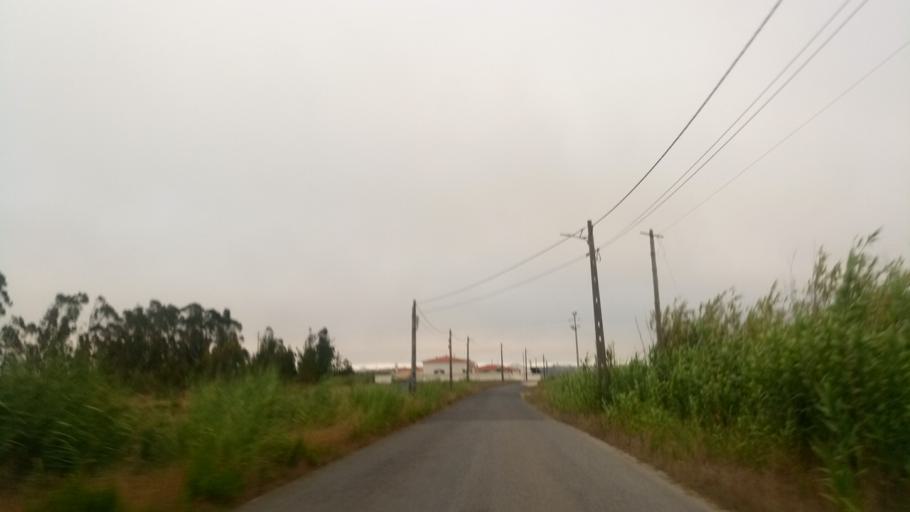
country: PT
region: Leiria
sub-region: Caldas da Rainha
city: Caldas da Rainha
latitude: 39.4398
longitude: -9.1574
